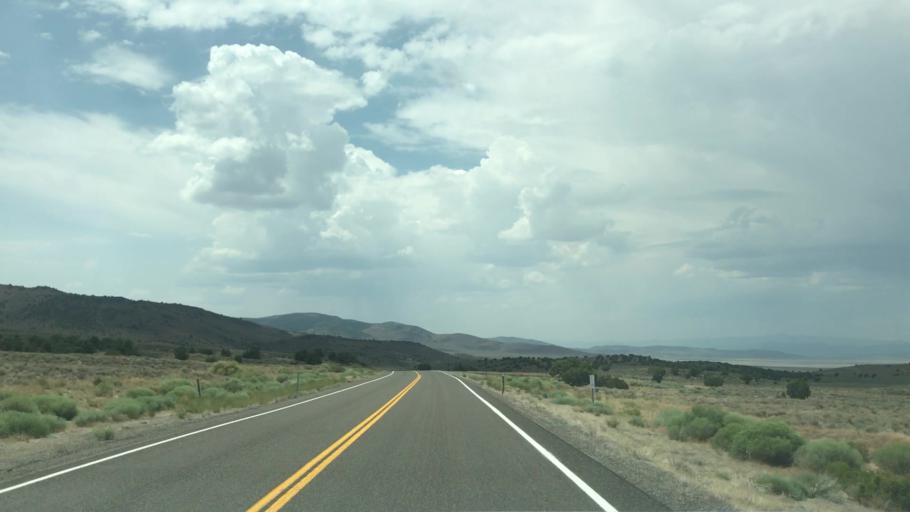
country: US
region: Nevada
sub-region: Eureka County
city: Eureka
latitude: 39.4079
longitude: -115.6980
